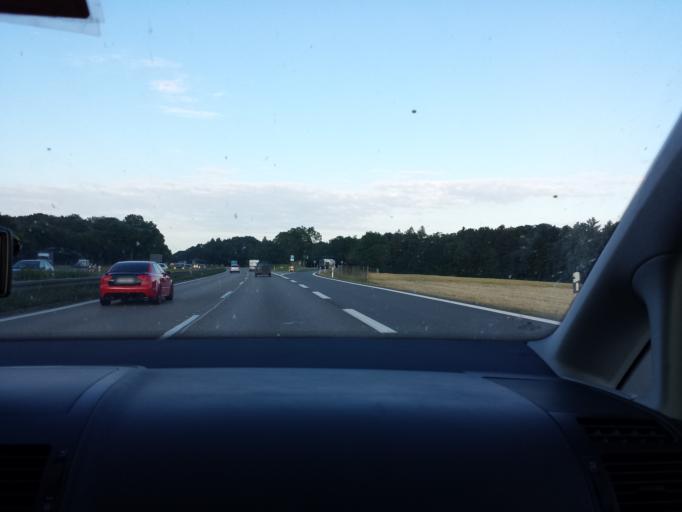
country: DE
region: Baden-Wuerttemberg
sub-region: Tuebingen Region
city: Bernstadt
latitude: 48.4531
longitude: 10.0522
